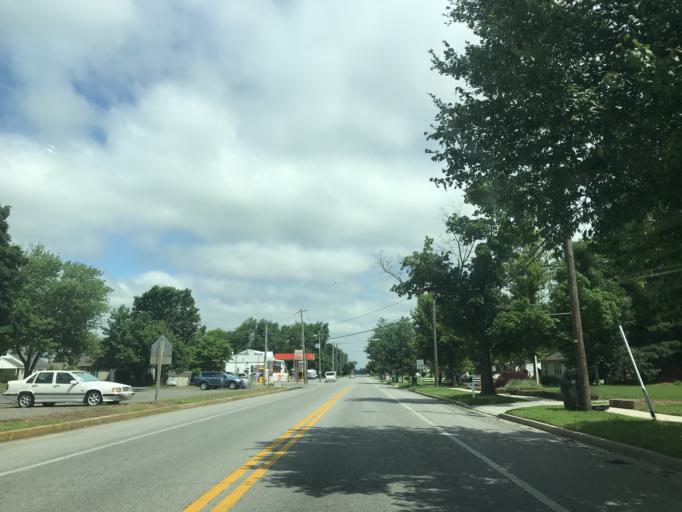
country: US
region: Maryland
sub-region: Caroline County
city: Ridgely
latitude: 38.9482
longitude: -75.8845
